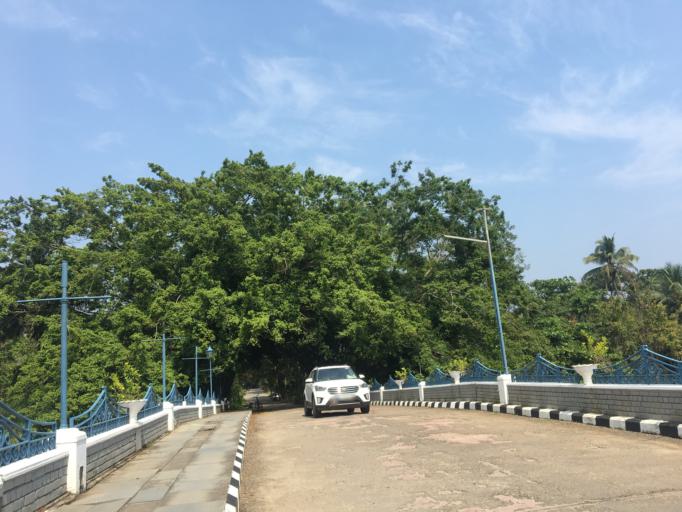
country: IN
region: Kerala
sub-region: Ernakulam
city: Cochin
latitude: 9.9613
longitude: 76.3223
